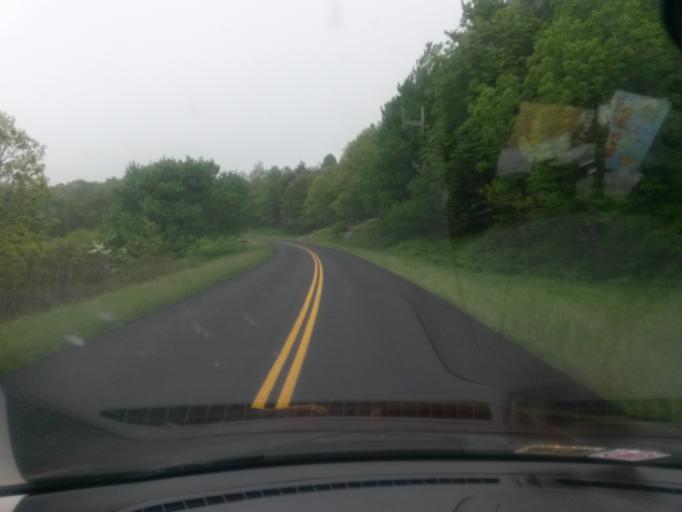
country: US
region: Virginia
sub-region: Floyd County
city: Floyd
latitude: 36.8028
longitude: -80.3743
